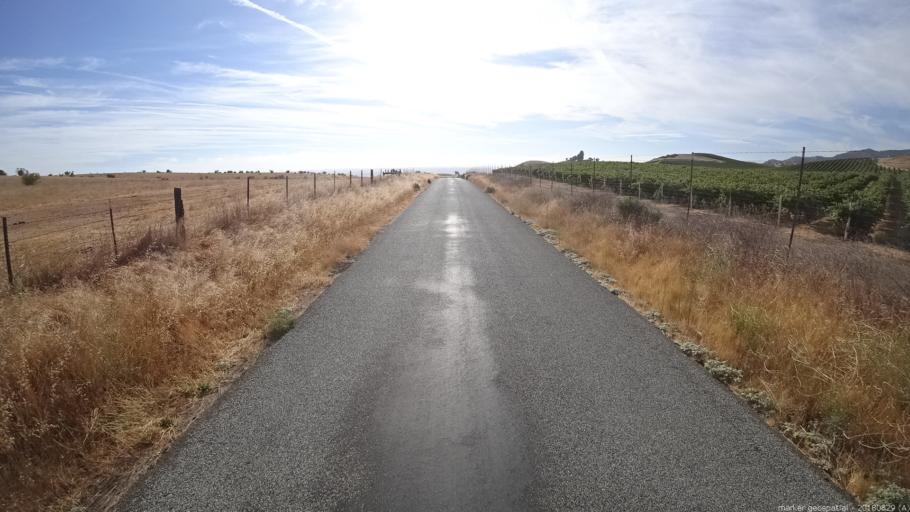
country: US
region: California
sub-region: Monterey County
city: King City
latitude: 36.0184
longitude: -120.9451
